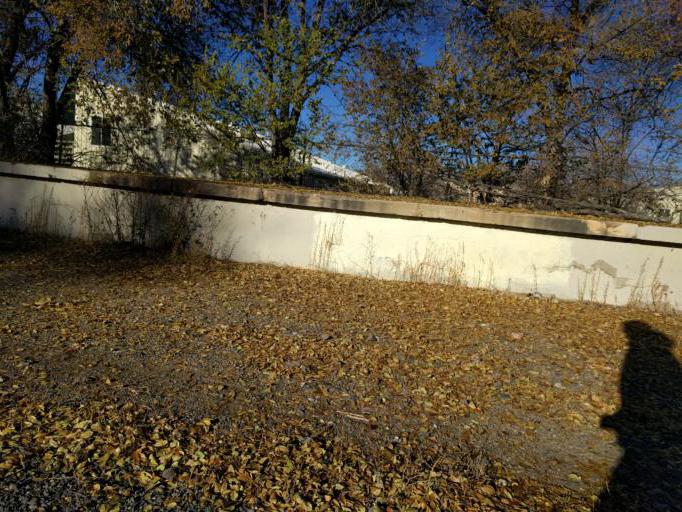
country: US
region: New Mexico
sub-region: Santa Fe County
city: Santa Fe
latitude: 35.6632
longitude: -105.9642
